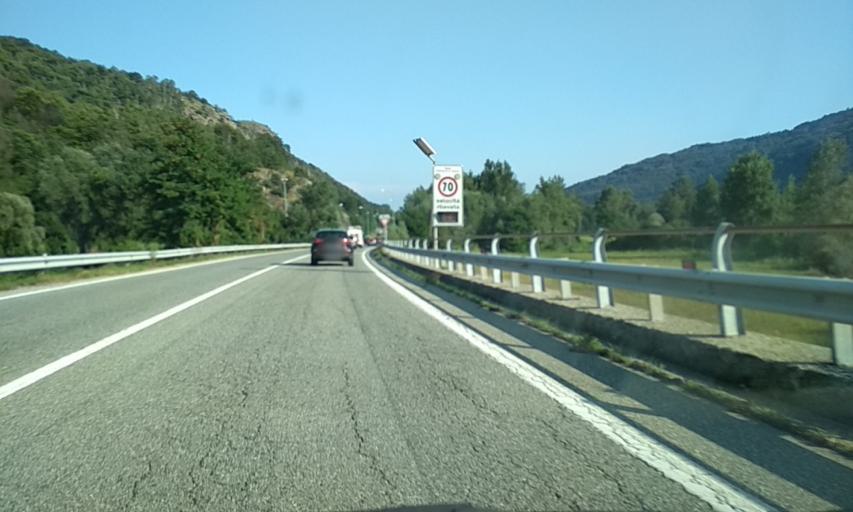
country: IT
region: Piedmont
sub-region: Provincia di Torino
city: Pont-Canavese
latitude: 45.4143
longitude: 7.6165
